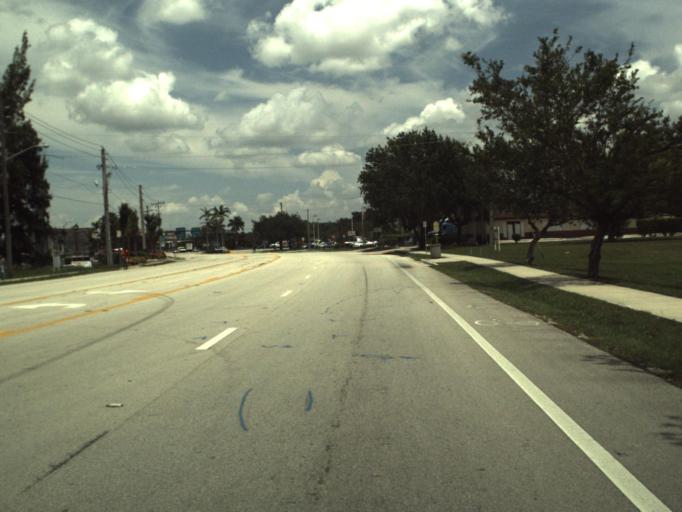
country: US
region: Florida
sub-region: Broward County
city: Coconut Creek
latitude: 26.2427
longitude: -80.1650
